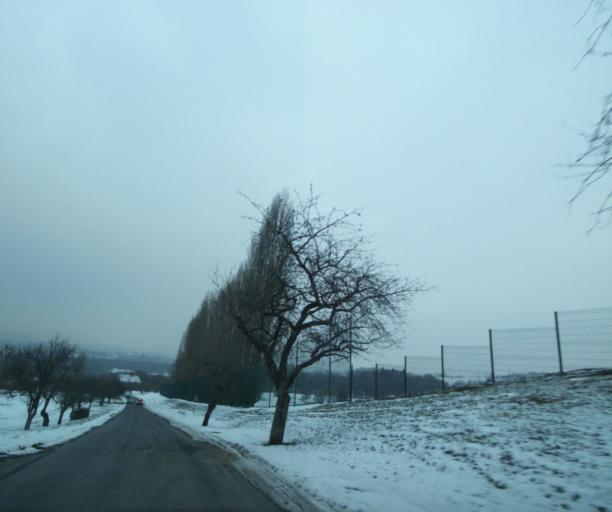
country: FR
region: Rhone-Alpes
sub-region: Departement de la Haute-Savoie
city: Reignier-Esery
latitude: 46.1429
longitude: 6.2419
